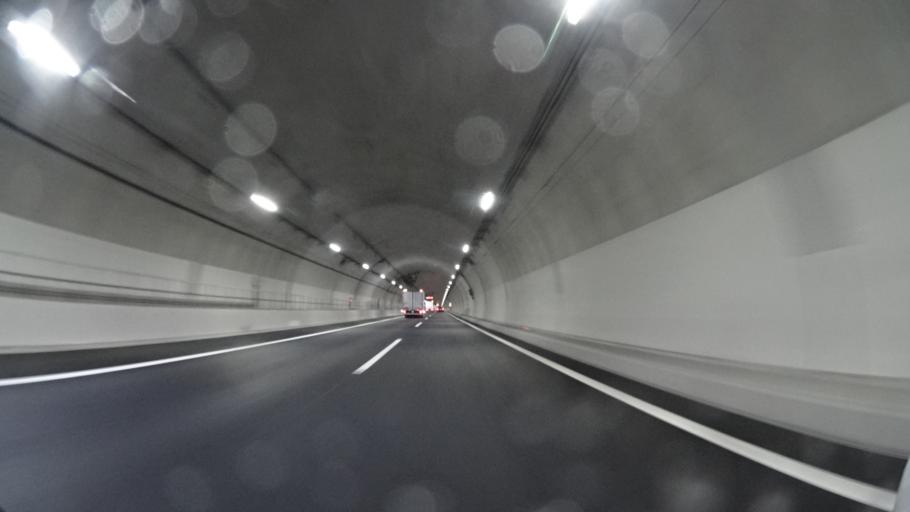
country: JP
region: Osaka
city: Ikeda
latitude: 34.8748
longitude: 135.4433
